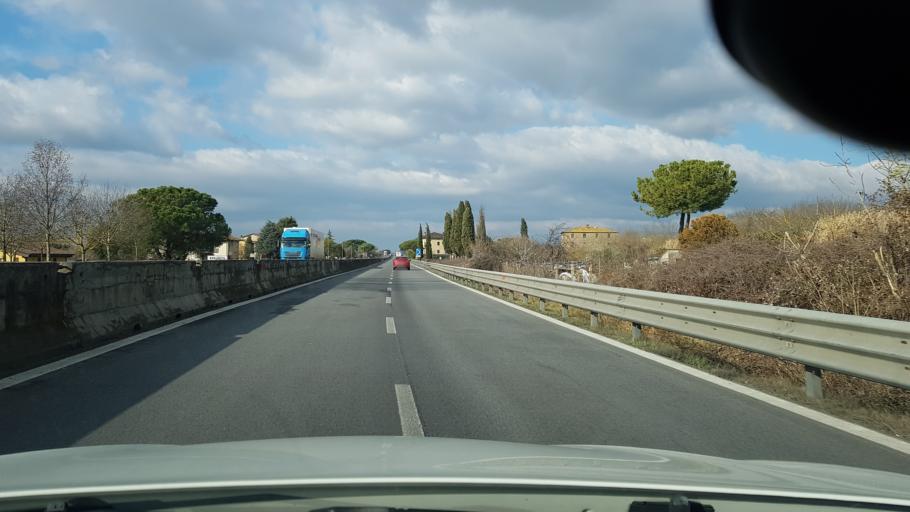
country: IT
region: Tuscany
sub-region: Province of Arezzo
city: Terontola
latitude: 43.1863
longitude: 12.0336
